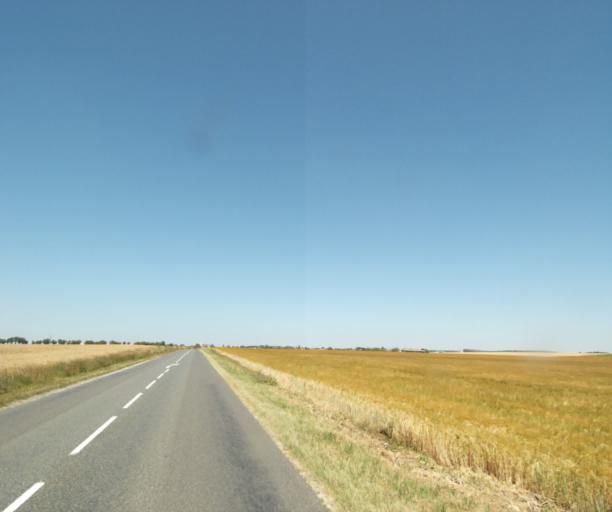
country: FR
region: Ile-de-France
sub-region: Departement de Seine-et-Marne
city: La Chapelle-la-Reine
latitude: 48.3056
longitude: 2.5583
